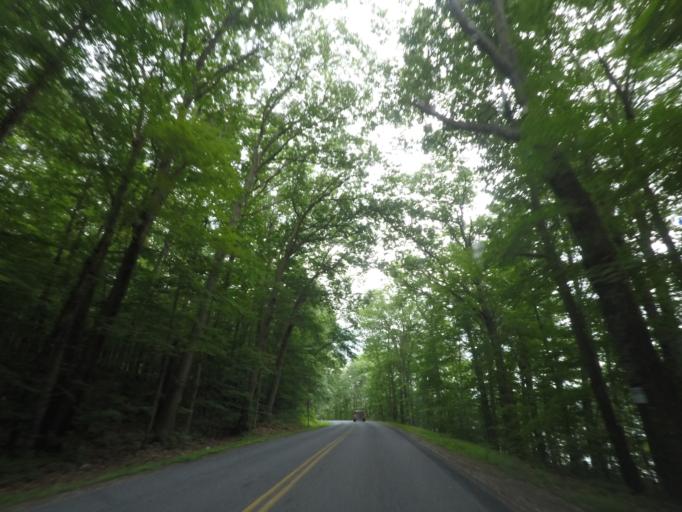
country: US
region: New York
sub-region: Saratoga County
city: Stillwater
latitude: 42.8435
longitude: -73.5372
